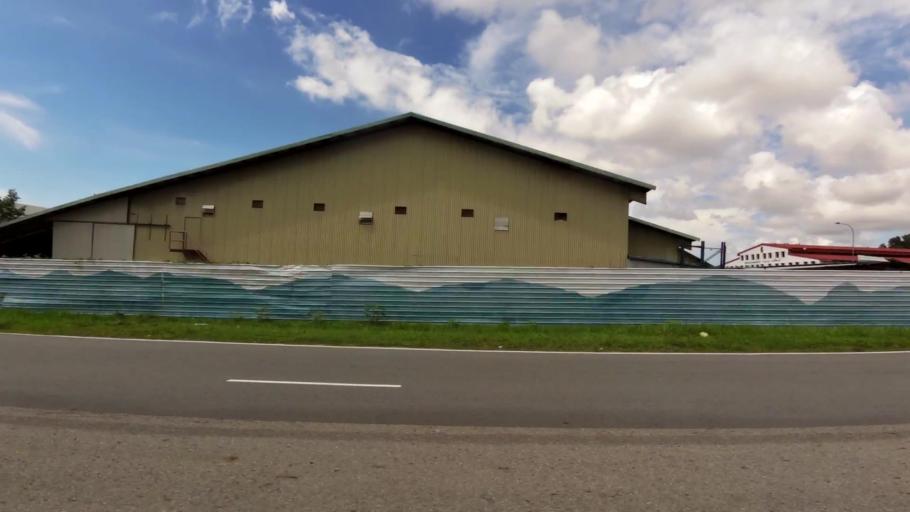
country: BN
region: Brunei and Muara
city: Bandar Seri Begawan
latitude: 4.9808
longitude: 114.9555
